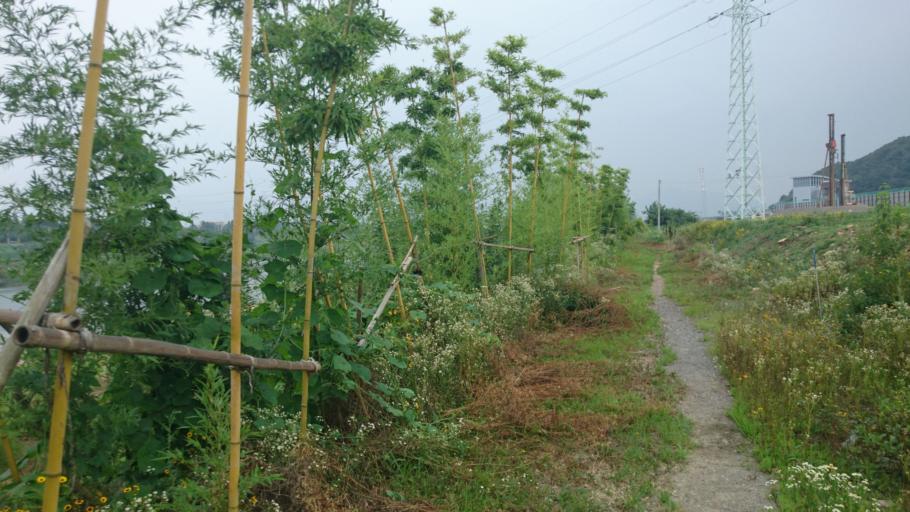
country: KR
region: Daegu
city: Hwawon
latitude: 35.8514
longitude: 128.4700
